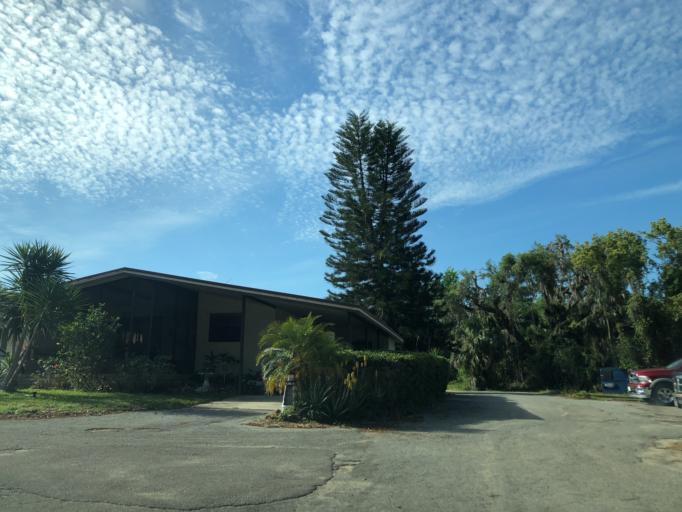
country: US
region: Florida
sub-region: Lake County
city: Astatula
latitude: 28.7230
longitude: -81.7424
